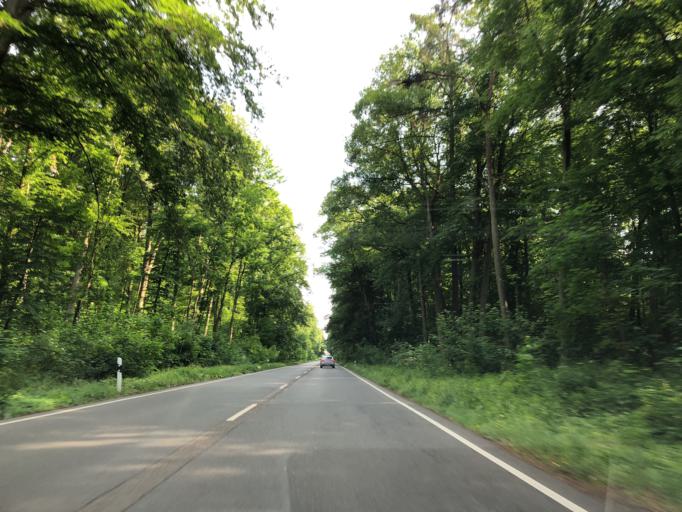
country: DE
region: Hesse
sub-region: Regierungsbezirk Darmstadt
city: Neu Isenburg
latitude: 50.0708
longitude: 8.6936
